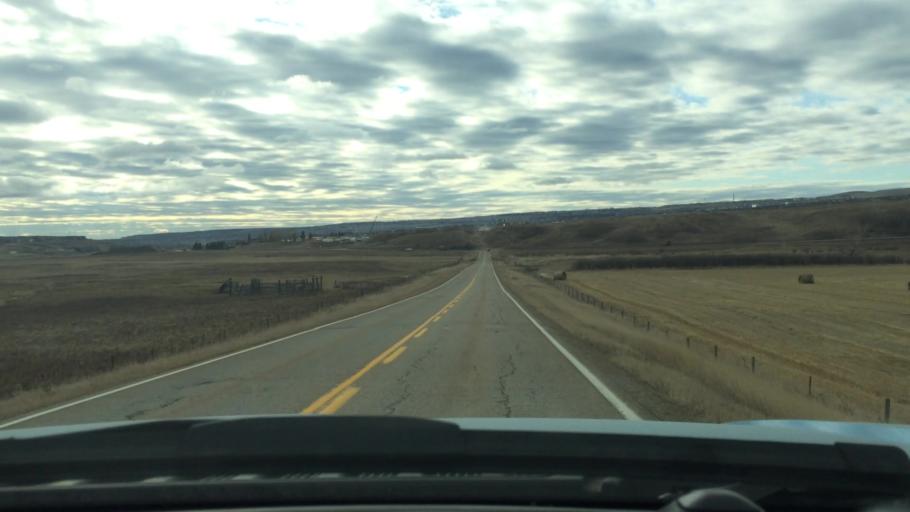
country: CA
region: Alberta
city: Airdrie
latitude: 51.1940
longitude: -114.1413
